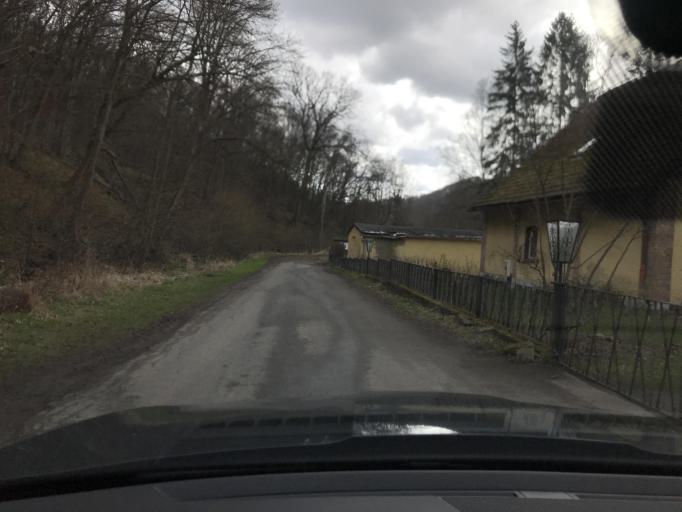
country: DE
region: Saxony-Anhalt
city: Harzgerode
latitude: 51.6746
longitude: 11.1905
